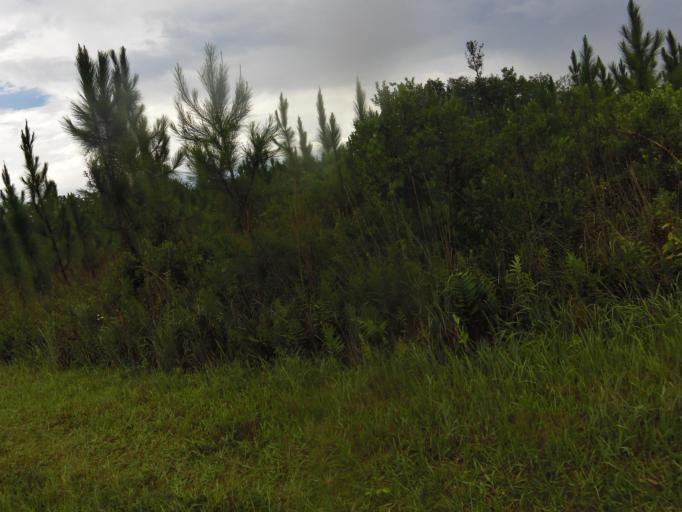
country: US
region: Florida
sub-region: Putnam County
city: Palatka
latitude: 29.6848
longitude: -81.7416
